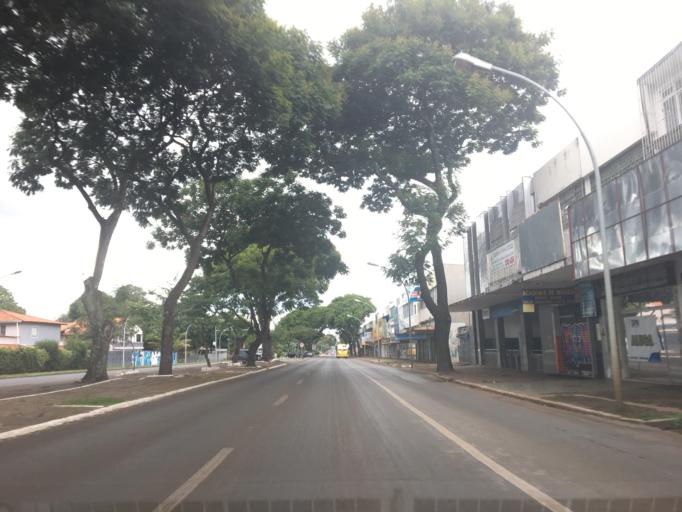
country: BR
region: Federal District
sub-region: Brasilia
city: Brasilia
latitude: -15.8231
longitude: -47.9209
